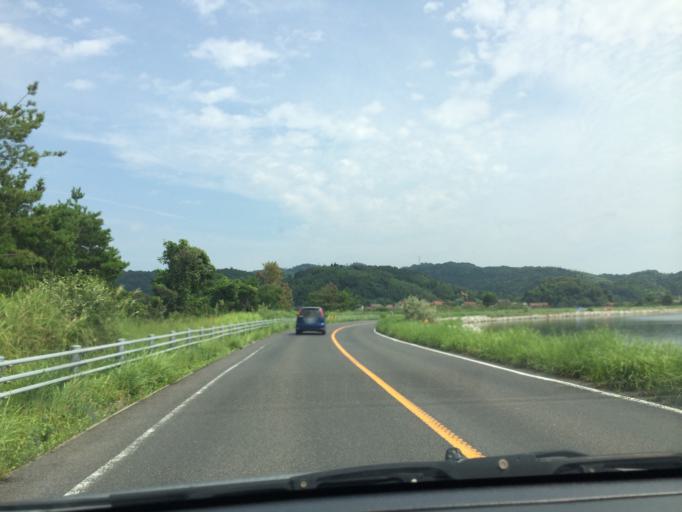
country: JP
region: Shimane
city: Sakaiminato
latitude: 35.5369
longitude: 133.1559
